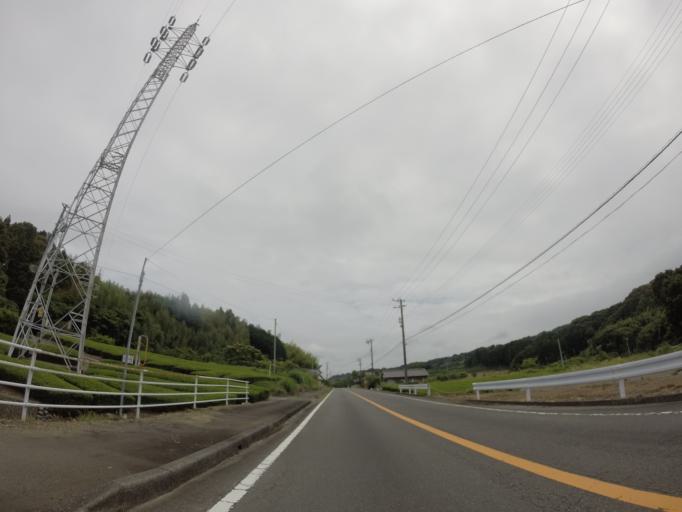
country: JP
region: Shizuoka
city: Shimada
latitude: 34.7821
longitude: 138.1629
